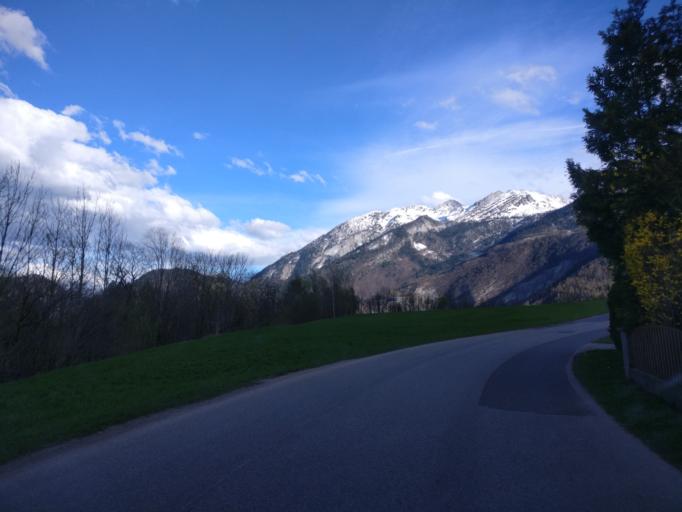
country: AT
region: Salzburg
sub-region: Politischer Bezirk Hallein
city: Golling an der Salzach
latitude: 47.5904
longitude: 13.1583
